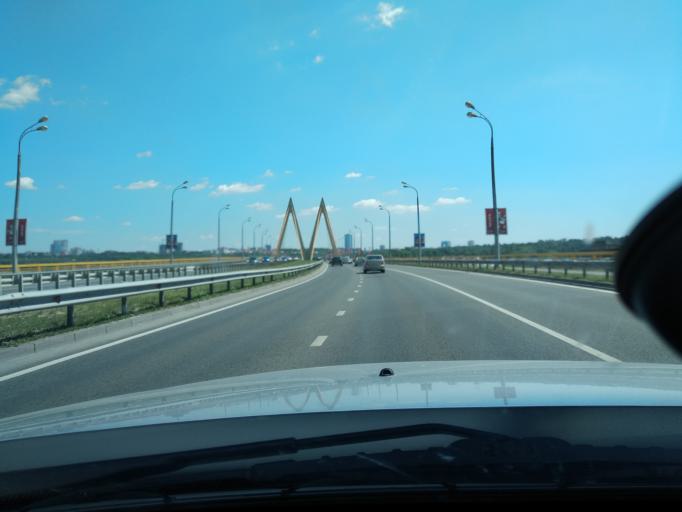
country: RU
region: Tatarstan
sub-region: Gorod Kazan'
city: Kazan
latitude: 55.8079
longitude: 49.1378
